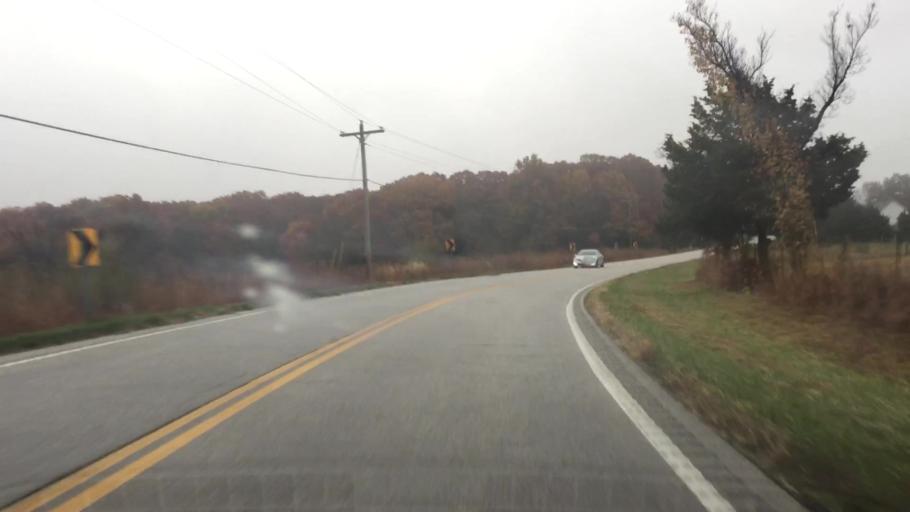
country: US
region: Missouri
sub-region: Callaway County
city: Fulton
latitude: 38.8769
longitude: -92.0745
